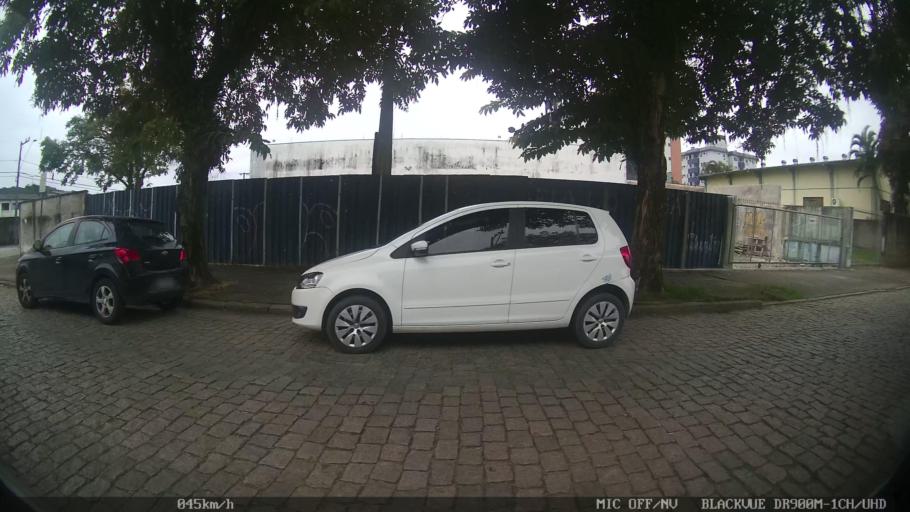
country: BR
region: Santa Catarina
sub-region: Joinville
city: Joinville
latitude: -26.3124
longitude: -48.8395
